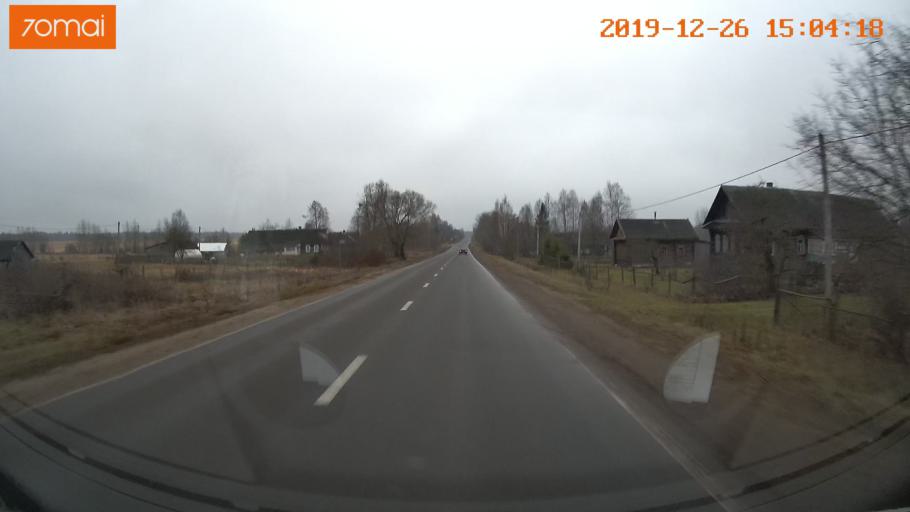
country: RU
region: Jaroslavl
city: Rybinsk
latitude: 58.2017
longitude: 38.8636
